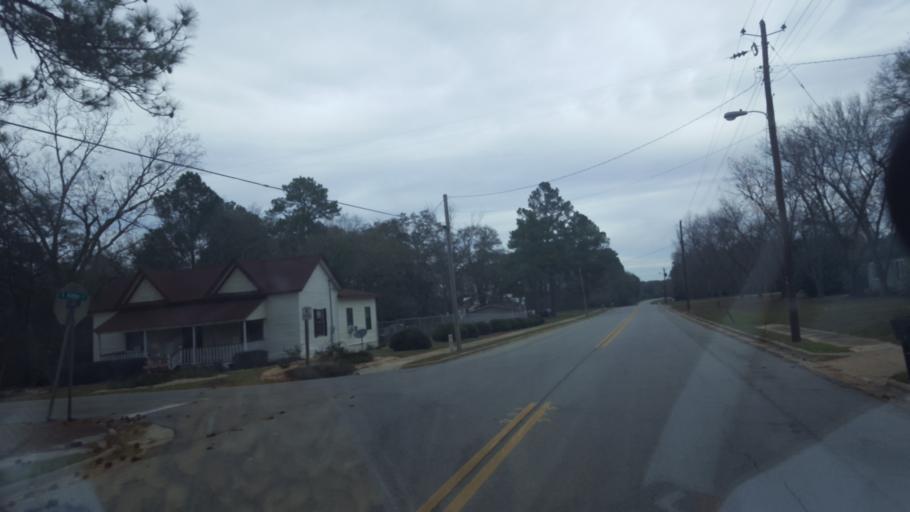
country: US
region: Georgia
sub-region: Wilcox County
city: Rochelle
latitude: 31.8091
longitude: -83.4843
